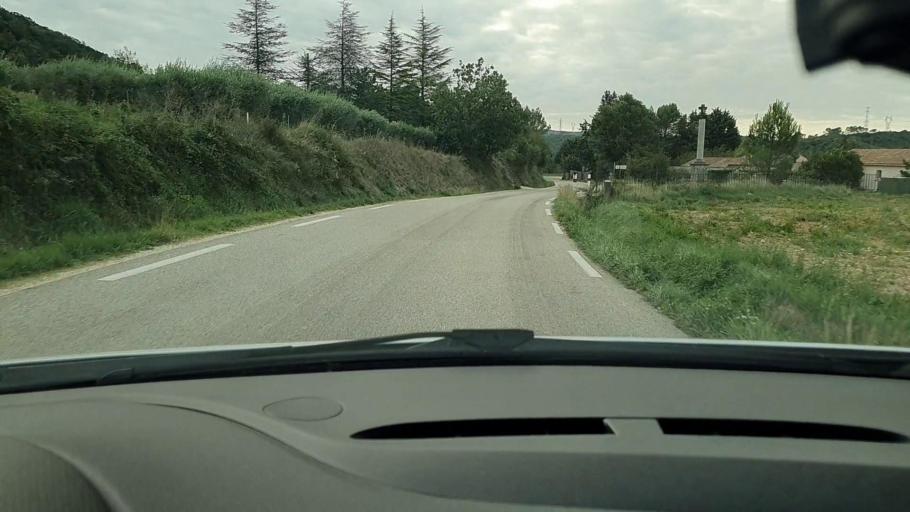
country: FR
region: Languedoc-Roussillon
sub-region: Departement du Gard
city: Mons
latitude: 44.1082
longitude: 4.2255
